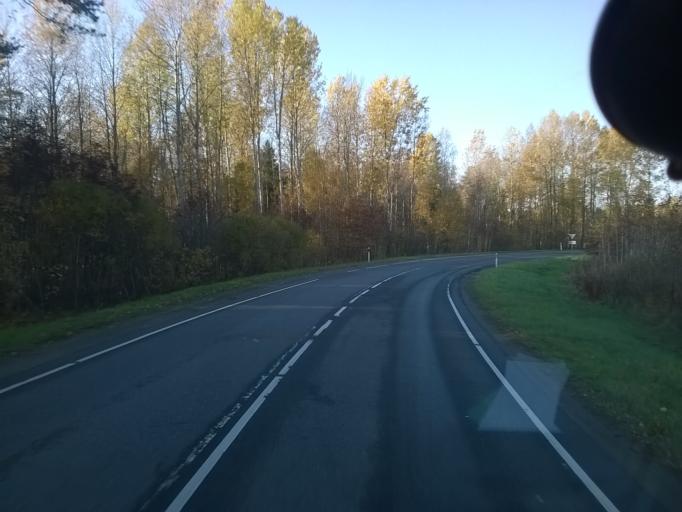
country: EE
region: Harju
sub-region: Saku vald
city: Saku
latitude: 59.3133
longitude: 24.6745
